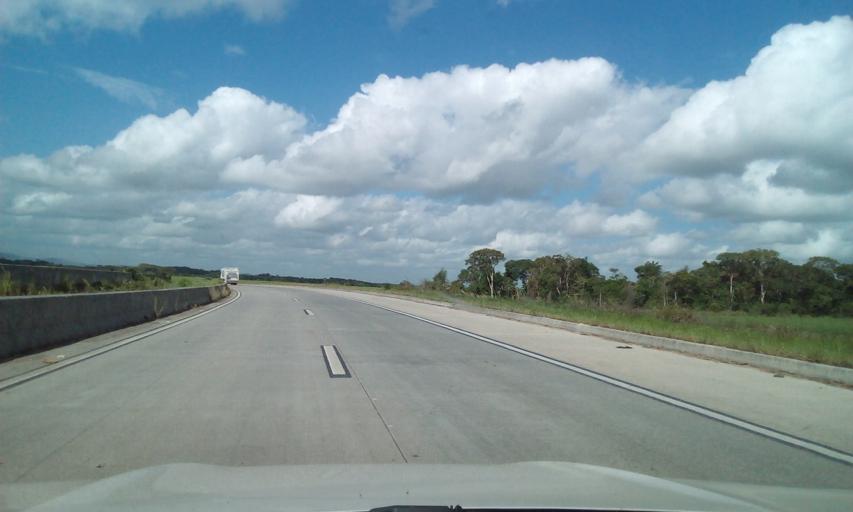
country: BR
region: Alagoas
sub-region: Messias
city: Messias
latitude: -9.3797
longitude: -35.8276
